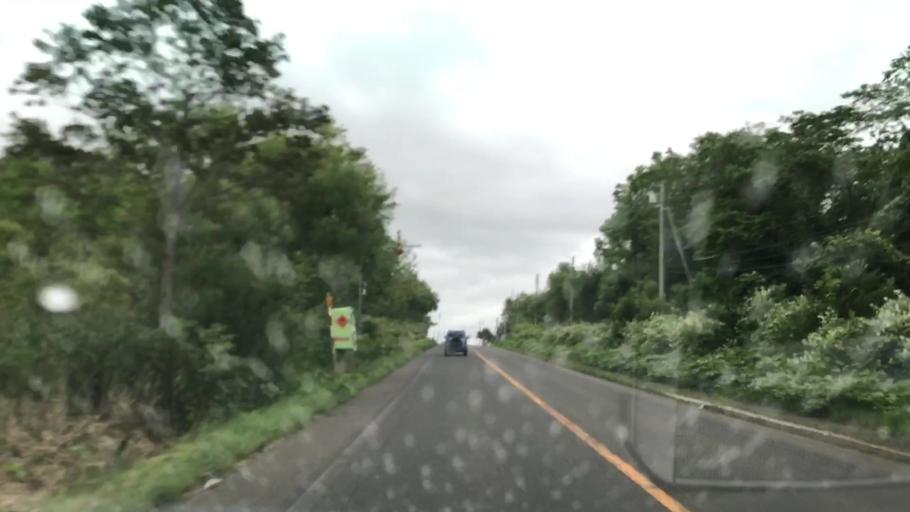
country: JP
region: Hokkaido
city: Niseko Town
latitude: 42.7961
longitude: 140.7505
